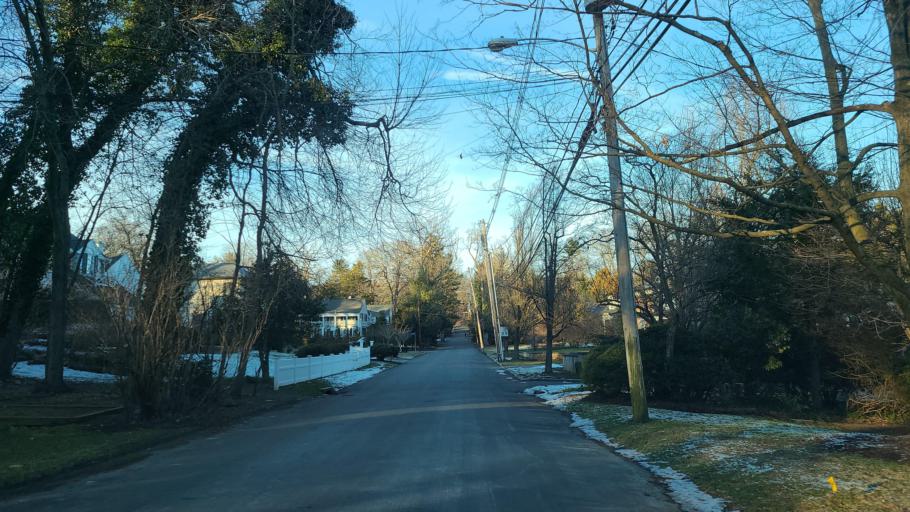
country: US
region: New Jersey
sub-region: Essex County
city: Short Hills
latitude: 40.7282
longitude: -74.3317
